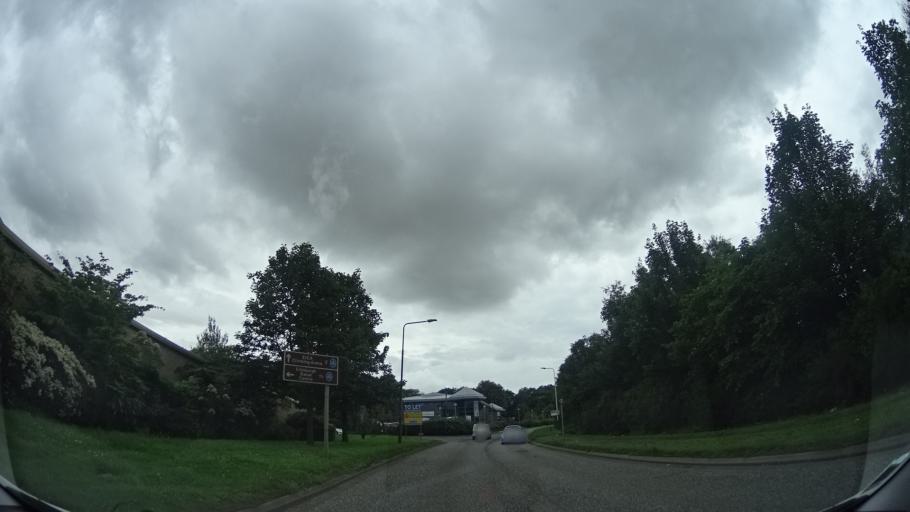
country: GB
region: Scotland
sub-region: Edinburgh
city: Newbridge
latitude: 55.9358
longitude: -3.4028
